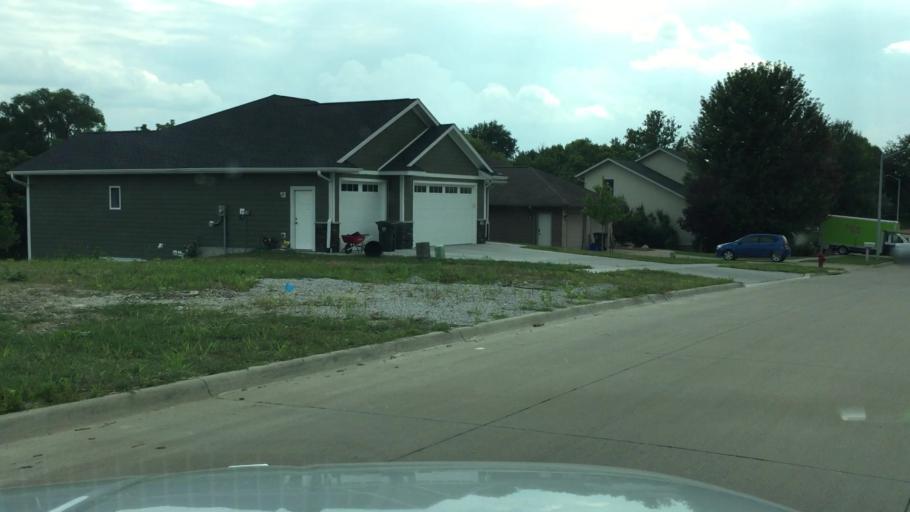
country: US
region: Iowa
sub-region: Johnson County
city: Iowa City
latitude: 41.6659
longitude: -91.4919
